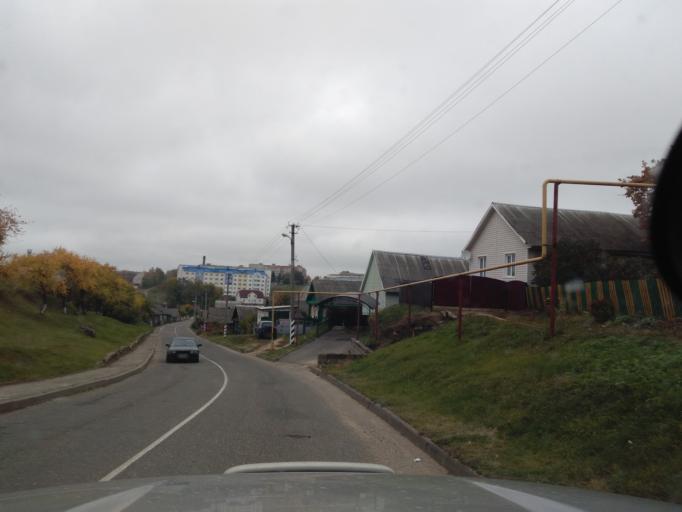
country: BY
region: Minsk
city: Kapyl'
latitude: 53.1456
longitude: 27.0938
